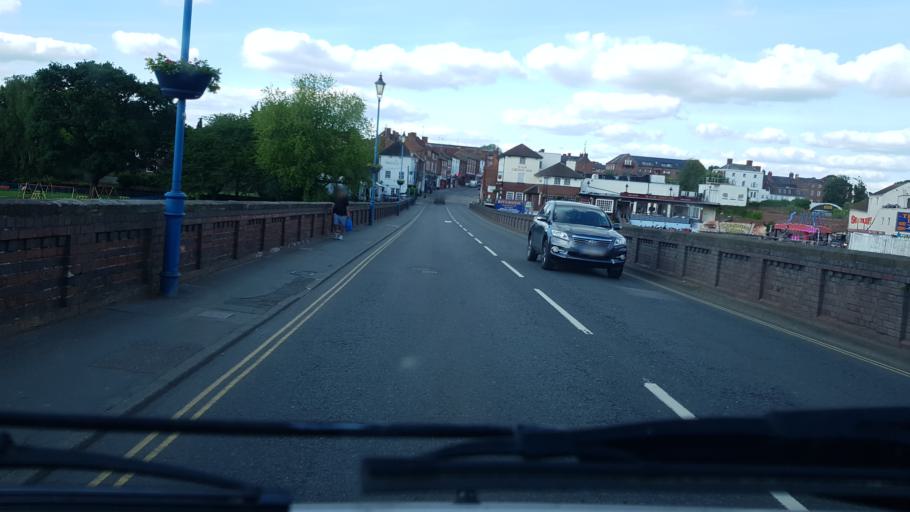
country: GB
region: England
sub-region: Worcestershire
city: Stourport-on-Severn
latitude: 52.3374
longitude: -2.2832
